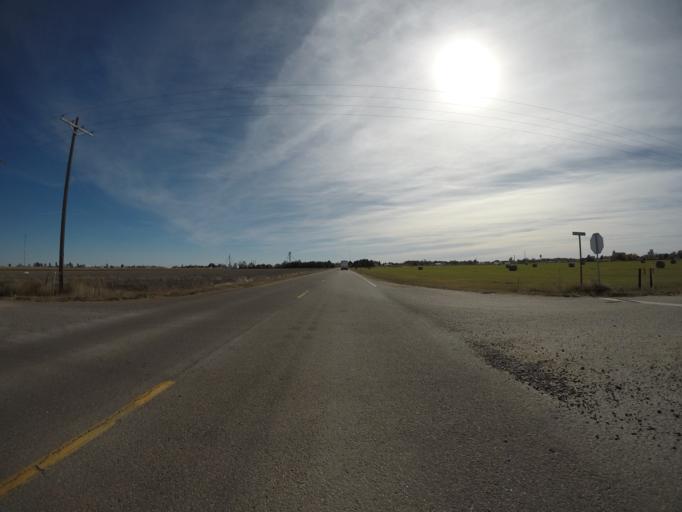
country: US
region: Colorado
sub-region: Kit Carson County
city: Burlington
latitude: 39.3157
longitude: -102.2601
